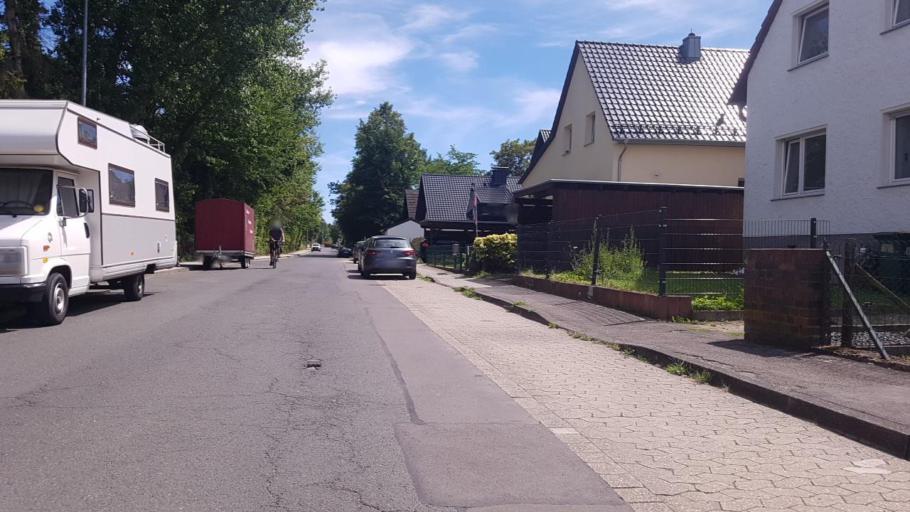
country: DE
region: North Rhine-Westphalia
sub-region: Regierungsbezirk Koln
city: Wachtberg
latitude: 50.6348
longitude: 7.0949
